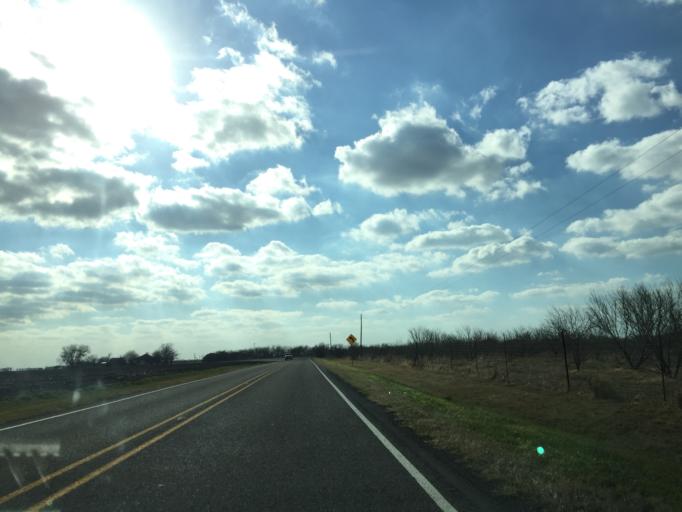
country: US
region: Texas
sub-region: Williamson County
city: Taylor
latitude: 30.6496
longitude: -97.3984
